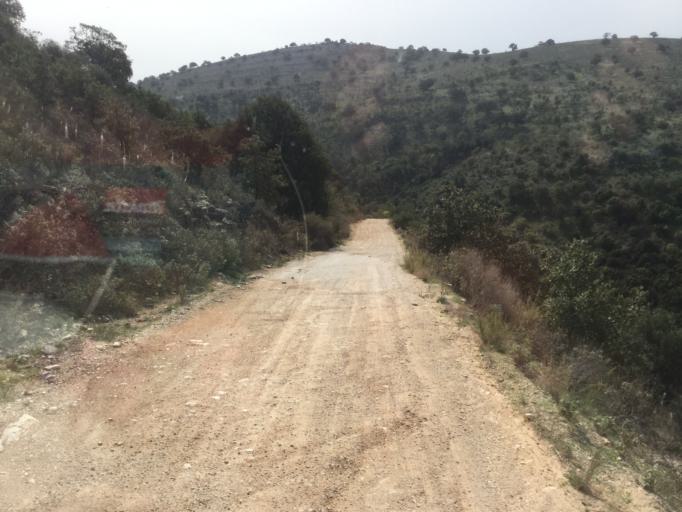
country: GR
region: West Greece
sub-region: Nomos Achaias
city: Lapas
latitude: 38.1761
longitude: 21.3745
